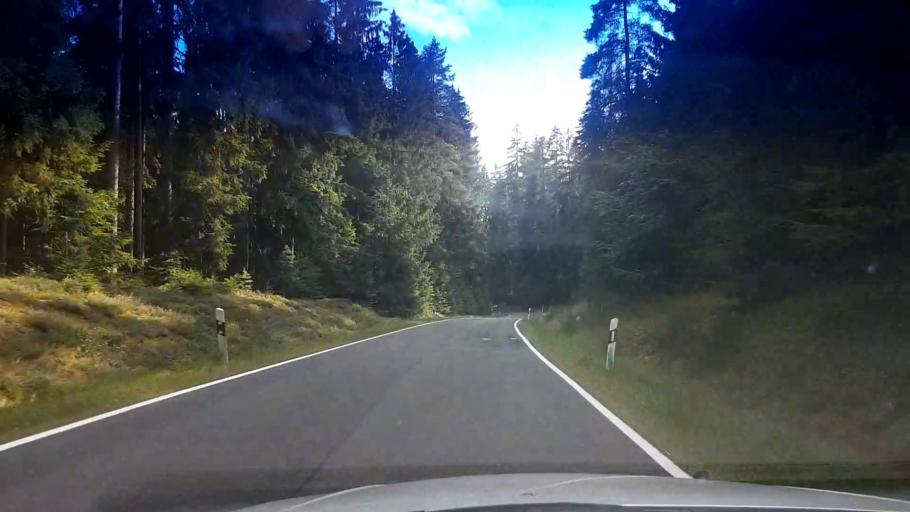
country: DE
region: Bavaria
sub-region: Upper Palatinate
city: Neualbenreuth
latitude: 49.9260
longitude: 12.4066
